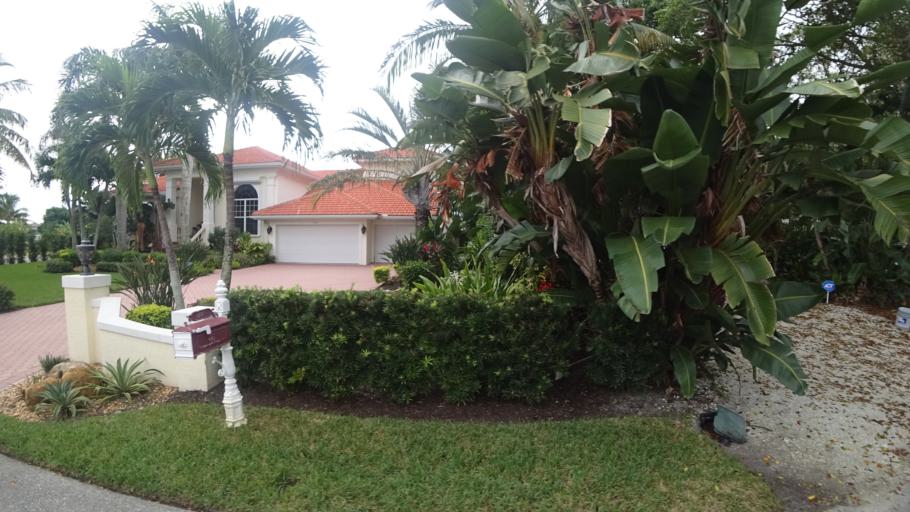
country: US
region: Florida
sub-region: Manatee County
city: Longboat Key
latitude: 27.4230
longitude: -82.6644
